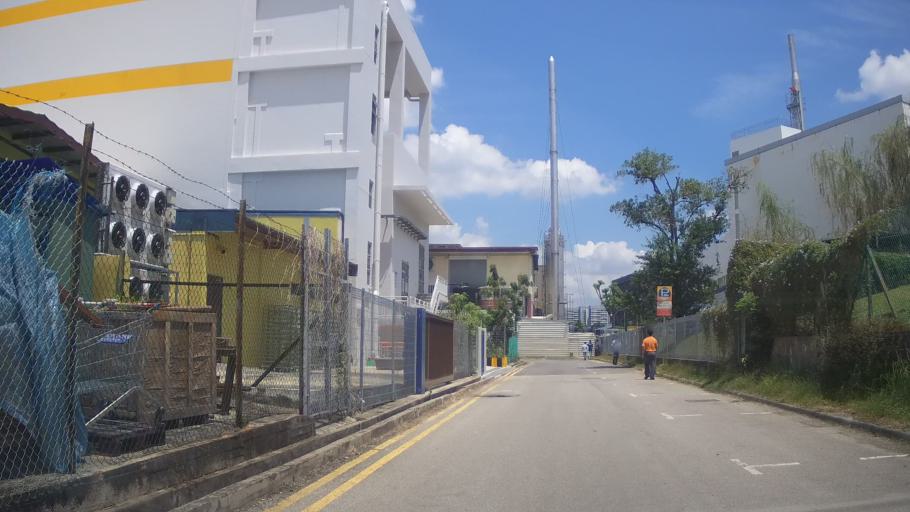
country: MY
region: Johor
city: Johor Bahru
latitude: 1.3339
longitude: 103.7111
